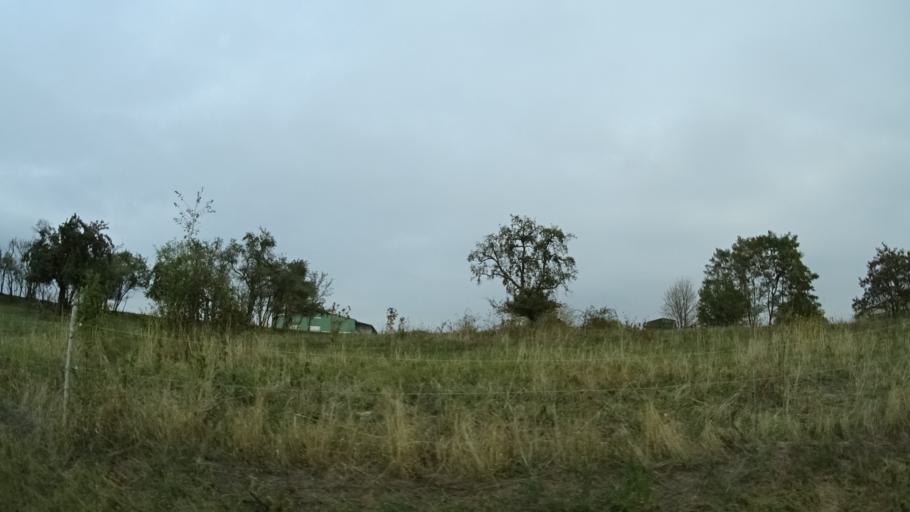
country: DE
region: Thuringia
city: Rippershausen
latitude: 50.6028
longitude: 10.3599
